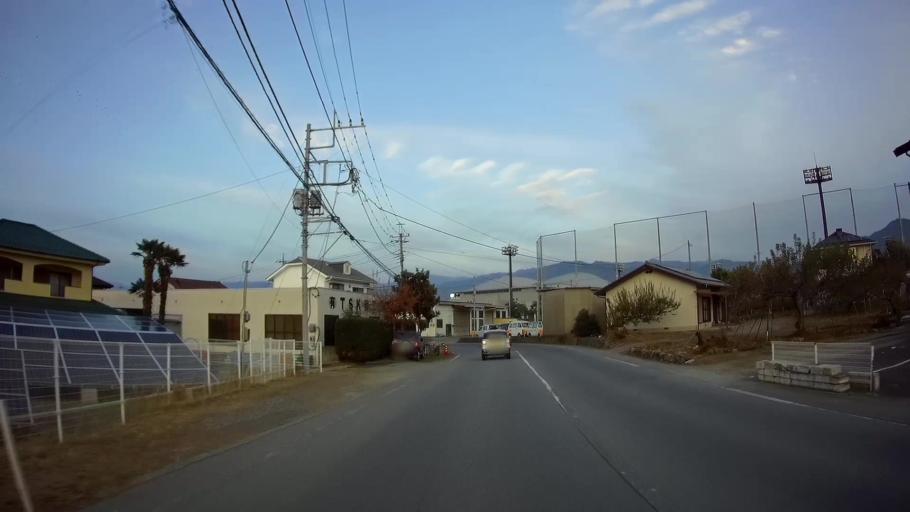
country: JP
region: Yamanashi
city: Isawa
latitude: 35.6484
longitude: 138.6879
